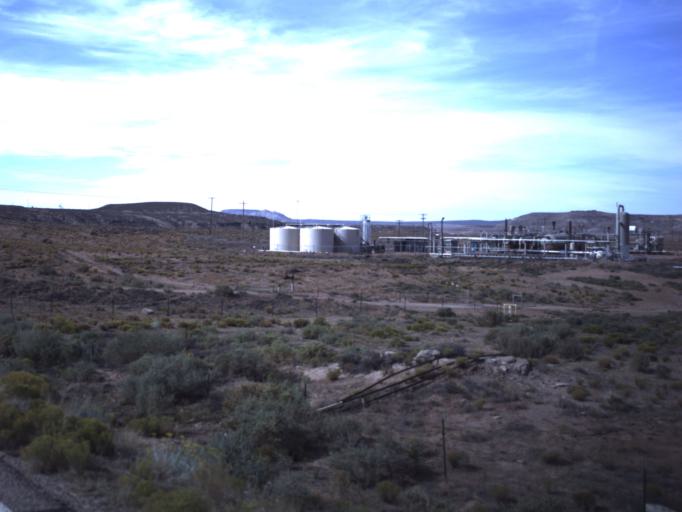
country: US
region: Utah
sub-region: San Juan County
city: Blanding
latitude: 37.2964
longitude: -109.2862
